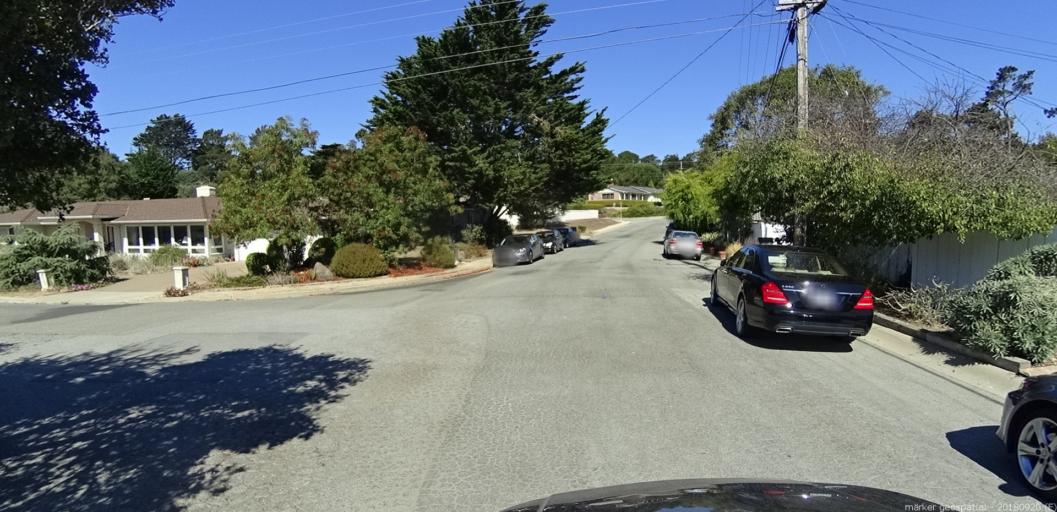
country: US
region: California
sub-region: Monterey County
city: Carmel-by-the-Sea
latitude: 36.5456
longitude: -121.9080
